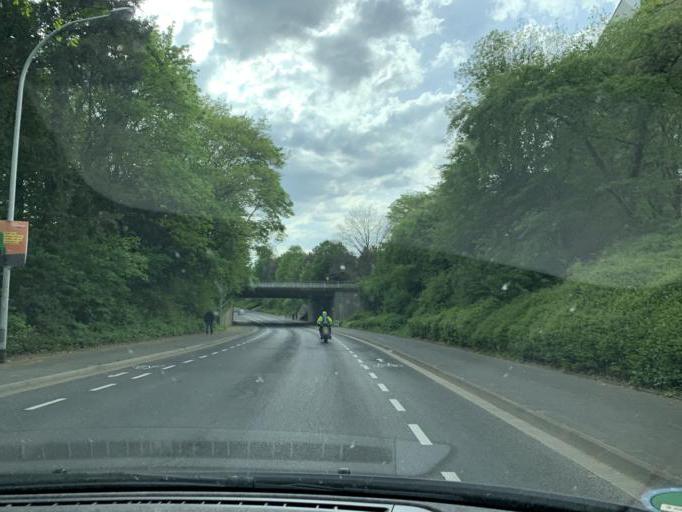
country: DE
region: North Rhine-Westphalia
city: Bruhl
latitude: 50.8321
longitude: 6.9017
